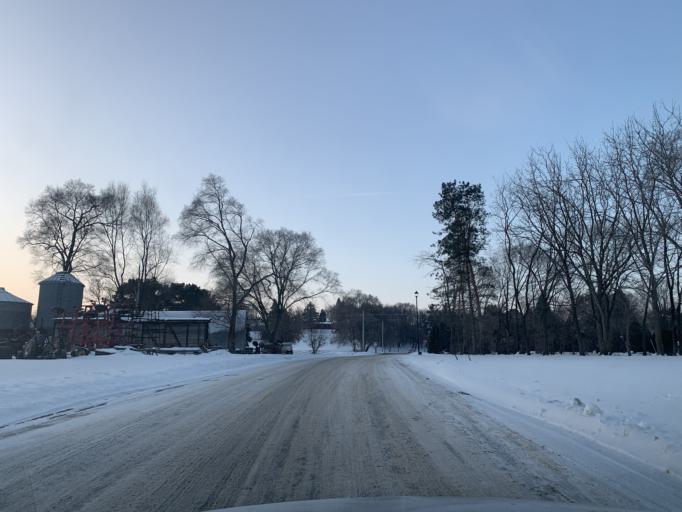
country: US
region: Minnesota
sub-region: Scott County
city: Shakopee
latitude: 44.7878
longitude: -93.4898
